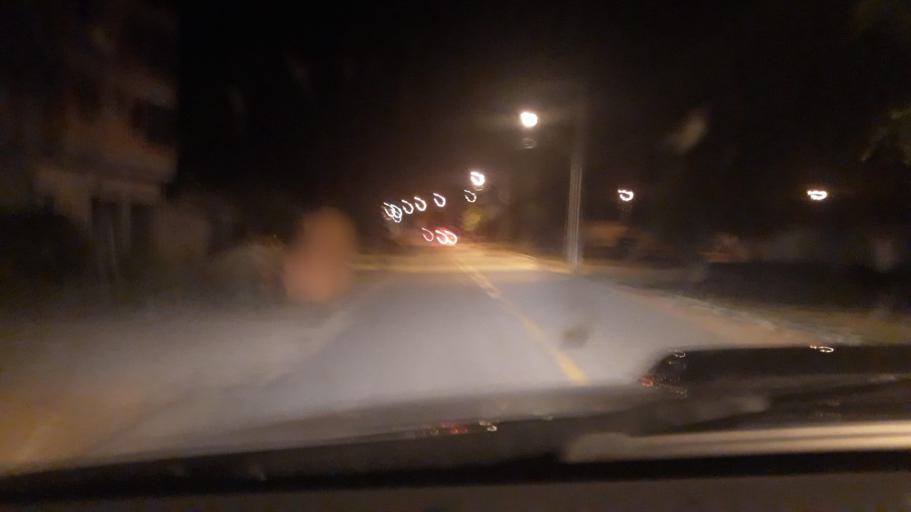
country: BR
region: Bahia
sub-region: Guanambi
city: Guanambi
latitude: -14.2859
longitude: -42.7103
